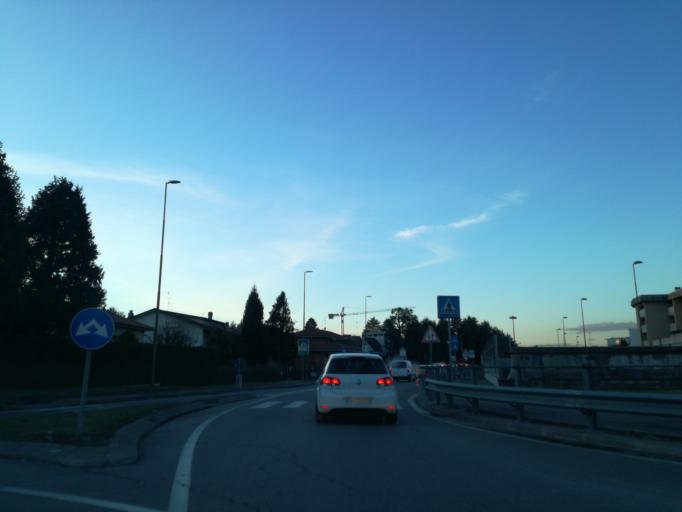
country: IT
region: Lombardy
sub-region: Provincia di Monza e Brianza
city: Vimercate
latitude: 45.6119
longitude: 9.3596
